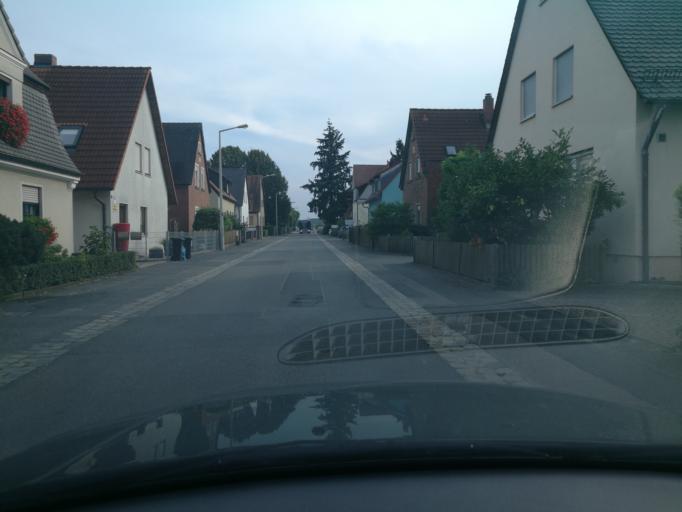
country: DE
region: Bavaria
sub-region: Regierungsbezirk Mittelfranken
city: Wetzendorf
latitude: 49.4880
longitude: 11.0611
